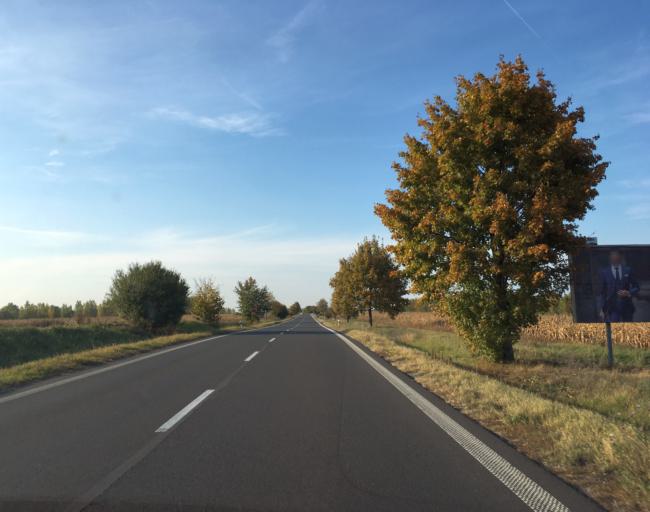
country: SK
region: Nitriansky
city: Surany
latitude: 48.0734
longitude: 18.0877
